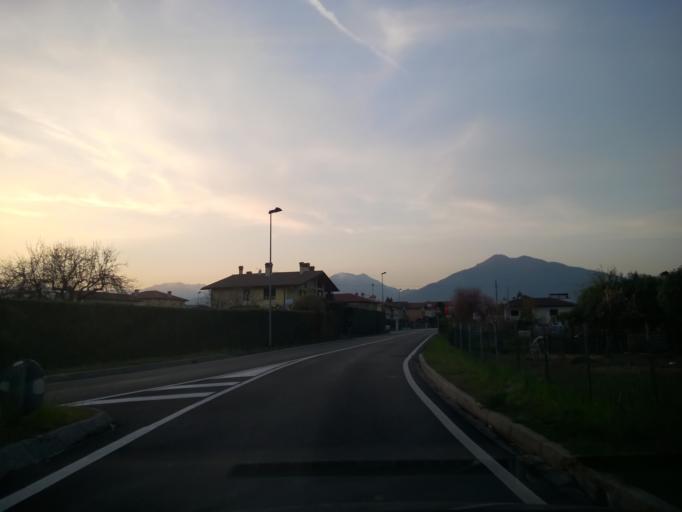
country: IT
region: Veneto
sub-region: Provincia di Vicenza
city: Marano Vicentino
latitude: 45.6899
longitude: 11.4444
